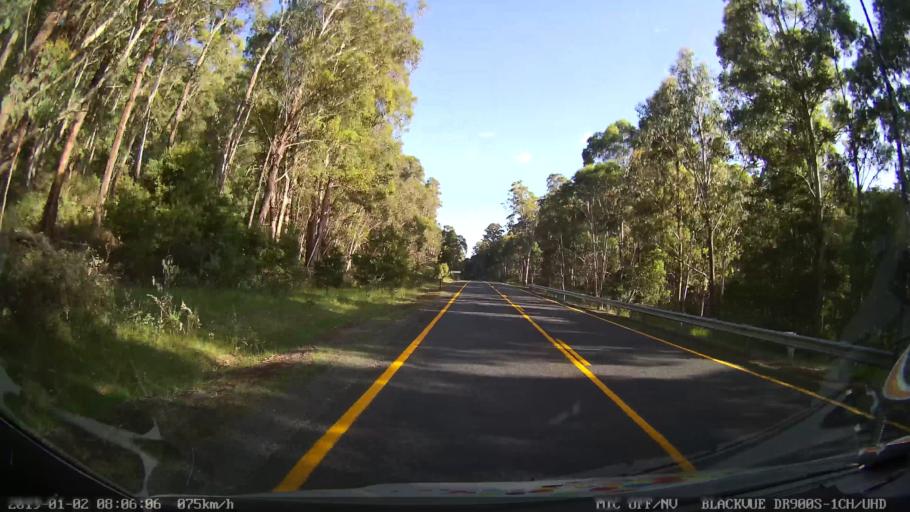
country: AU
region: New South Wales
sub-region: Tumut Shire
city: Tumut
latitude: -35.6438
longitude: 148.3872
